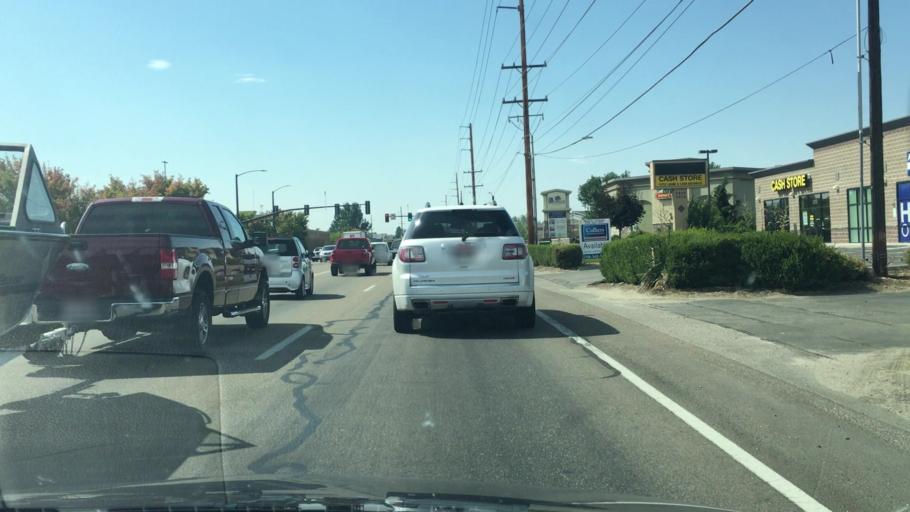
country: US
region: Idaho
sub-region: Ada County
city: Garden City
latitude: 43.6694
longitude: -116.2807
